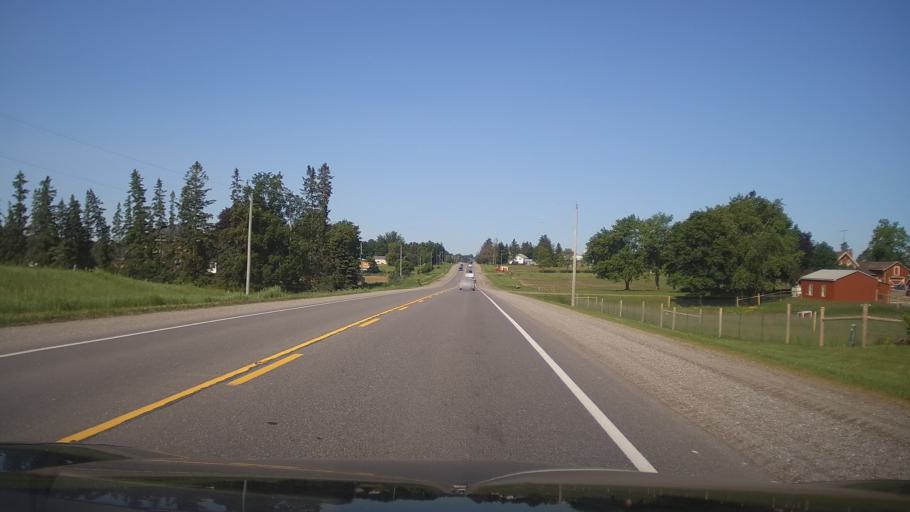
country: CA
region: Ontario
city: Omemee
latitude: 44.3428
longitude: -78.8359
